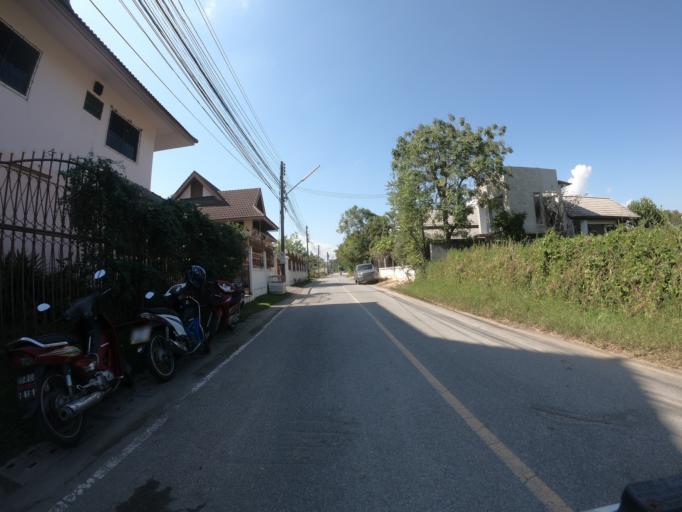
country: TH
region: Chiang Mai
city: Chiang Mai
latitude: 18.7436
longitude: 98.9686
